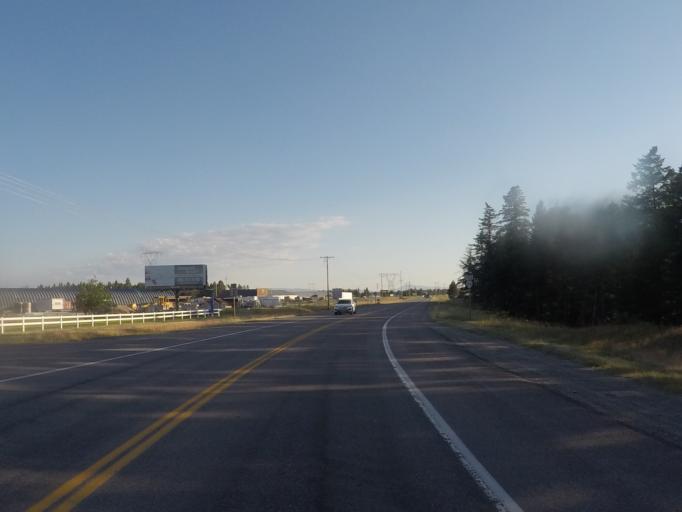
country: US
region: Montana
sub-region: Flathead County
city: Columbia Falls
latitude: 48.3626
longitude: -114.1503
